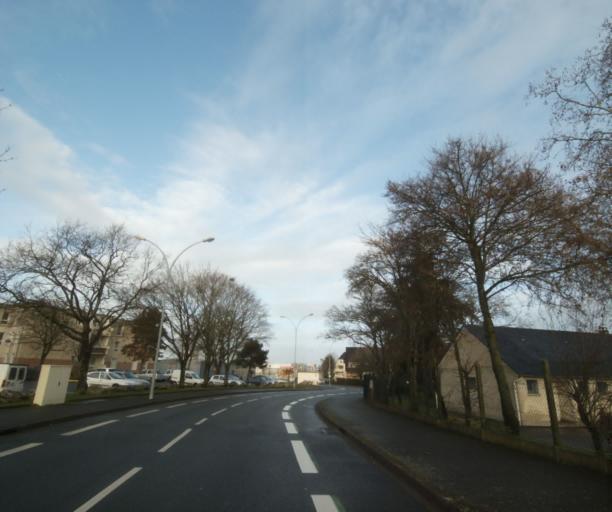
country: FR
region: Pays de la Loire
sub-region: Departement de la Sarthe
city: Le Mans
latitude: 47.9715
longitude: 0.2225
